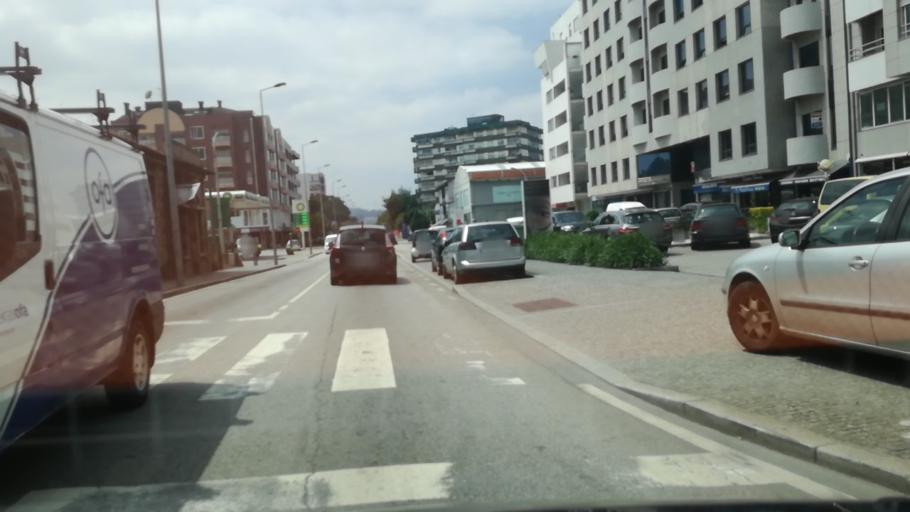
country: PT
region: Porto
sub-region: Trofa
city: Bougado
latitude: 41.3354
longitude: -8.5608
